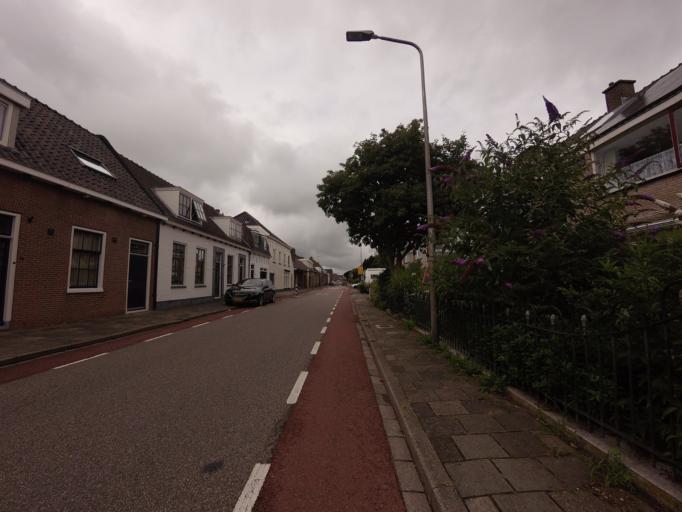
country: NL
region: South Holland
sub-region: Gemeente Alphen aan den Rijn
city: Alphen aan den Rijn
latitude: 52.1307
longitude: 4.6045
